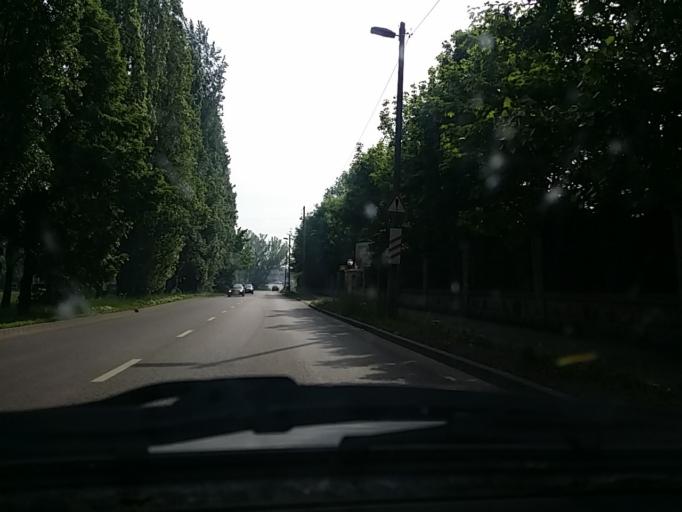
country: HU
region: Budapest
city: Budapest XIII. keruelet
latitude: 47.5419
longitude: 19.0651
